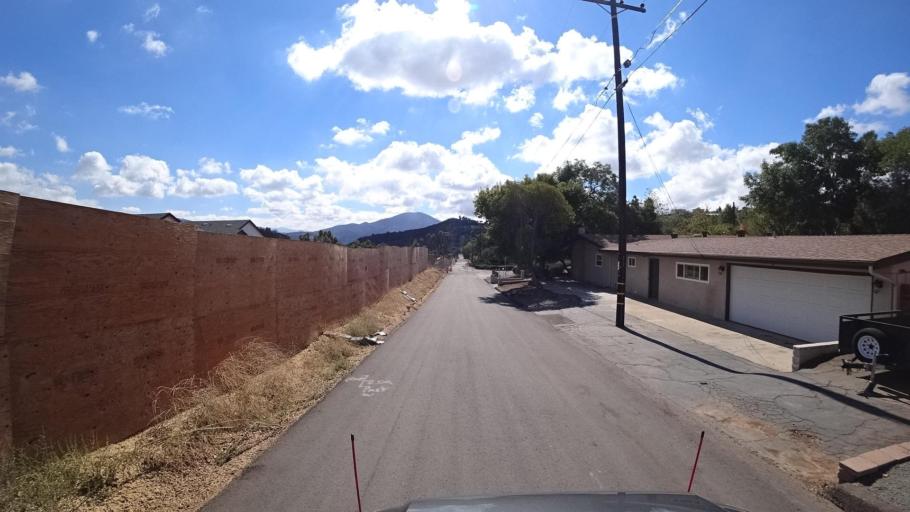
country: US
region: California
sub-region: San Diego County
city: Rancho San Diego
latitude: 32.7605
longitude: -116.9451
